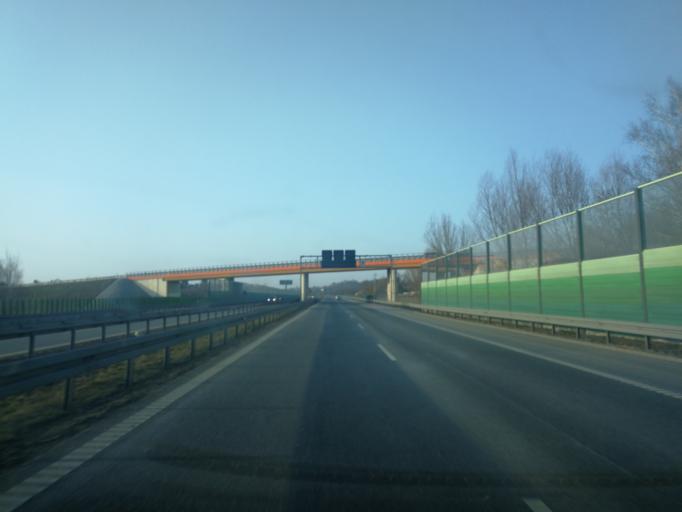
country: PL
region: Warmian-Masurian Voivodeship
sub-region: Powiat elblaski
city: Gronowo Gorne
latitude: 54.1314
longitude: 19.4579
